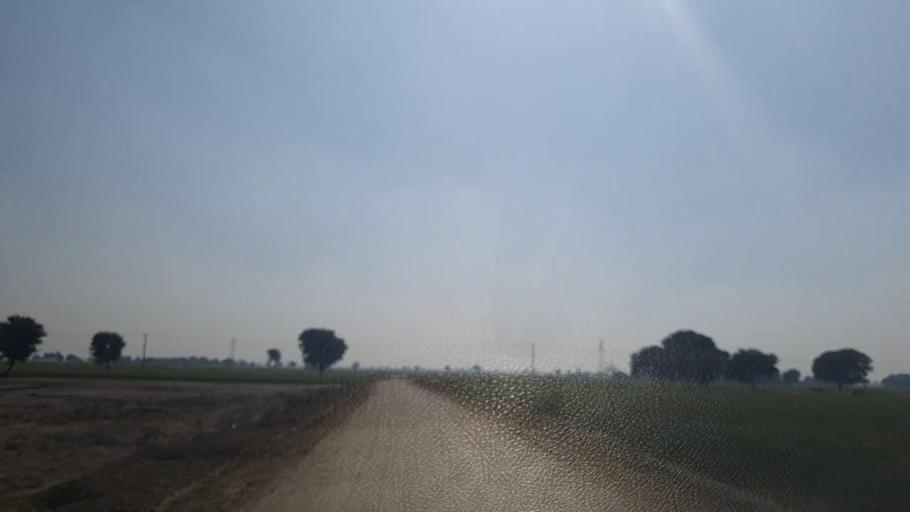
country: PK
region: Sindh
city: Shahpur Chakar
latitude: 26.1920
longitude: 68.5442
